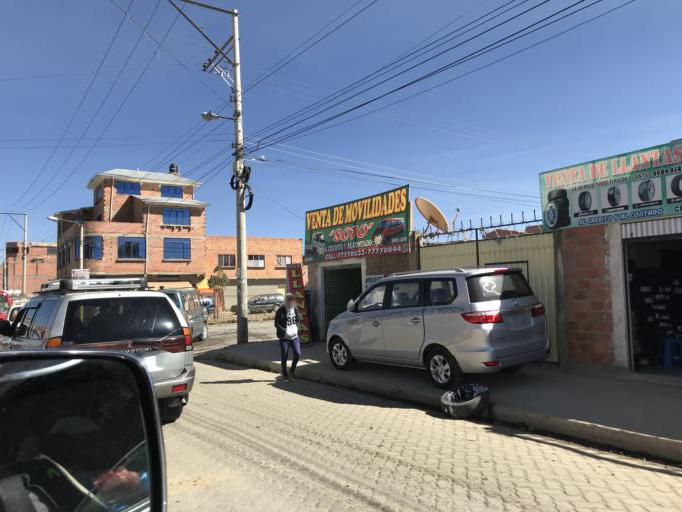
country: BO
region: La Paz
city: La Paz
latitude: -16.4862
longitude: -68.2012
